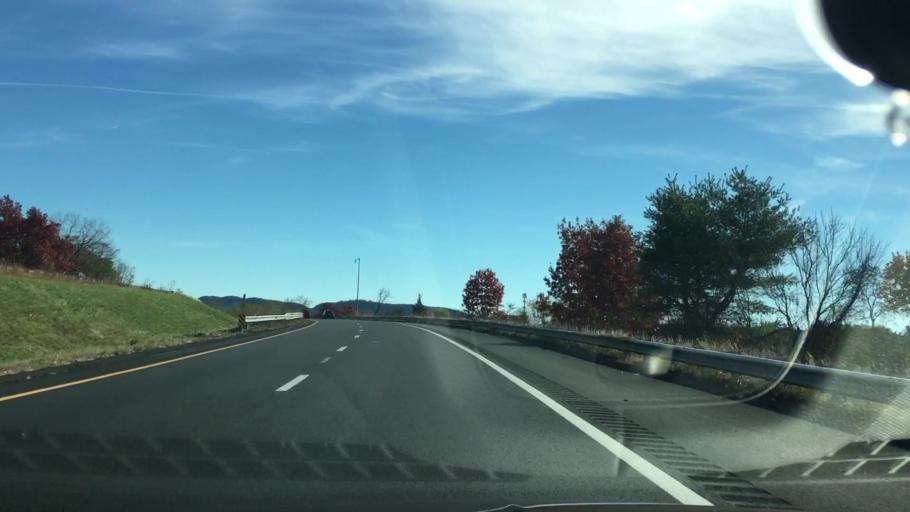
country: US
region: Massachusetts
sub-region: Hampshire County
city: Northampton
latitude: 42.3413
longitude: -72.6400
